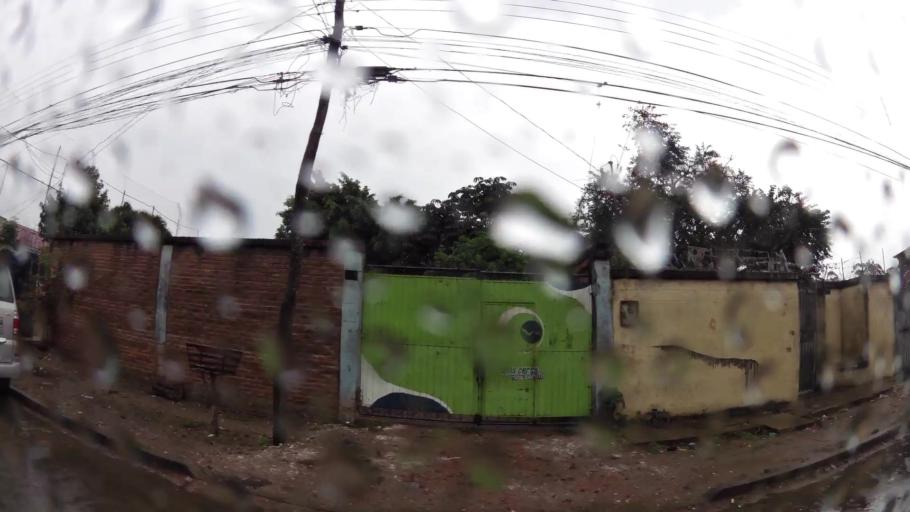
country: BO
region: Santa Cruz
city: Santa Cruz de la Sierra
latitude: -17.7999
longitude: -63.2240
